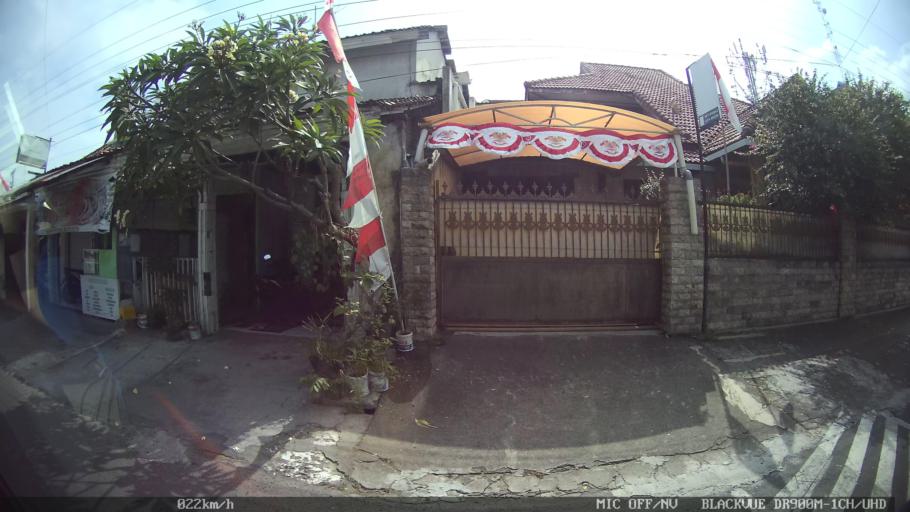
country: ID
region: Daerah Istimewa Yogyakarta
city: Depok
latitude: -7.7631
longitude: 110.4223
